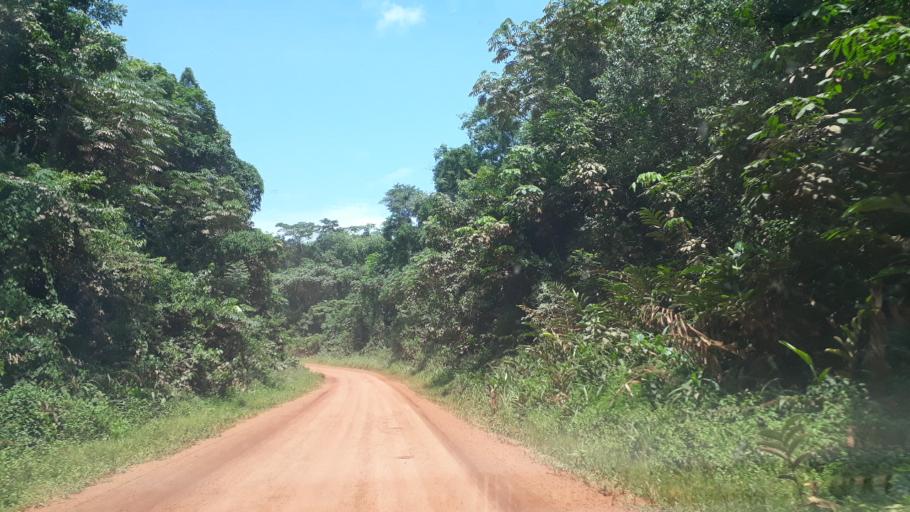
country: CD
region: Eastern Province
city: Kisangani
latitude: 0.5524
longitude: 25.8801
